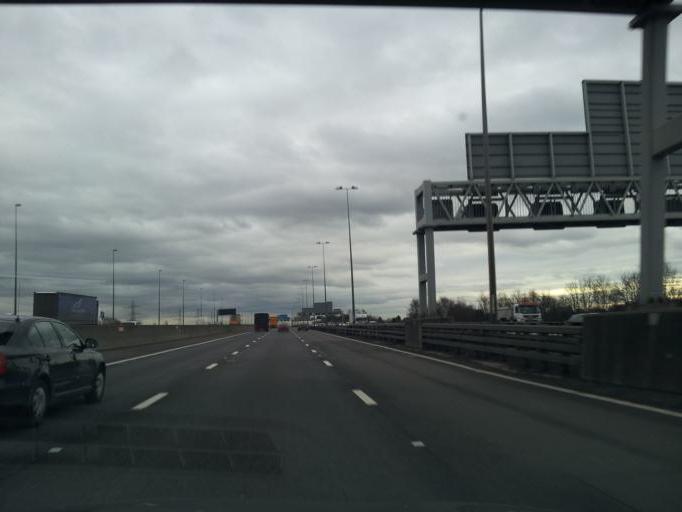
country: GB
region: England
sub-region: Warwickshire
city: Curdworth
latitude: 52.5237
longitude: -1.7281
